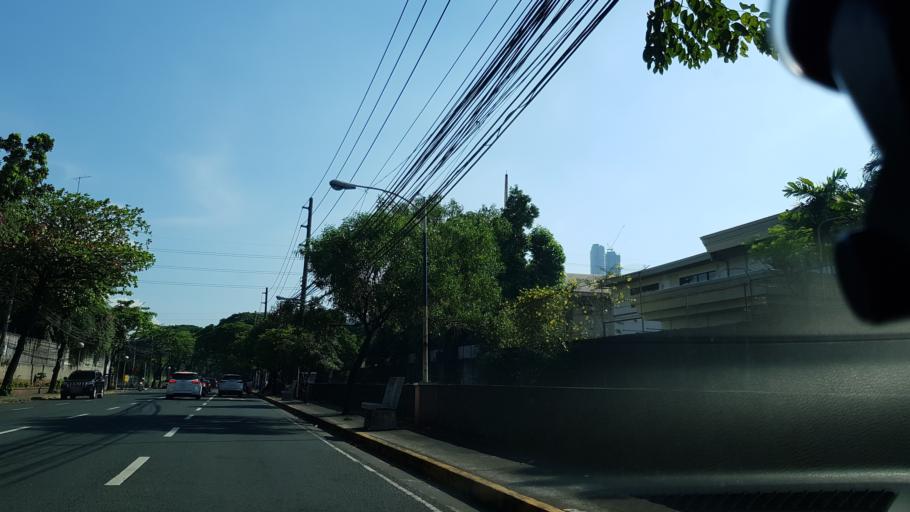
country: PH
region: Metro Manila
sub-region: Pasig
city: Pasig City
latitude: 14.5853
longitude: 121.0710
